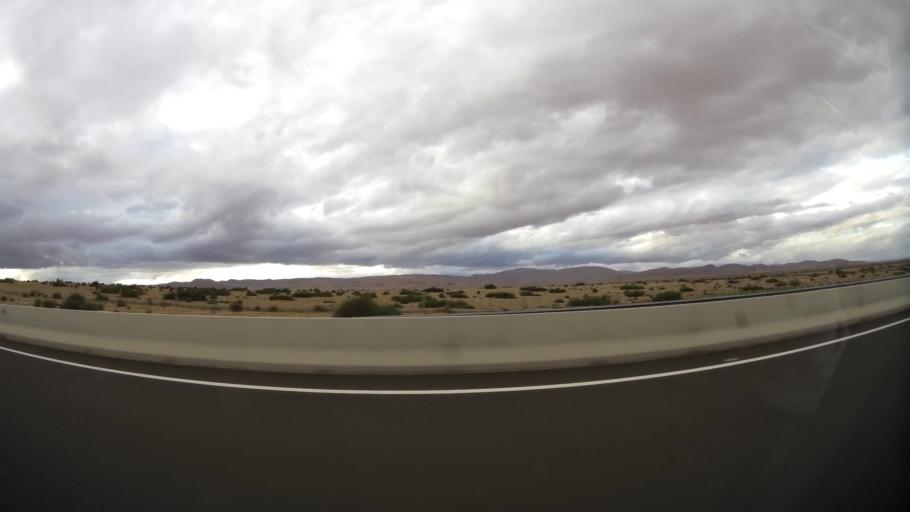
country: MA
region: Taza-Al Hoceima-Taounate
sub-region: Taza
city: Guercif
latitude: 34.3051
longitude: -3.6327
